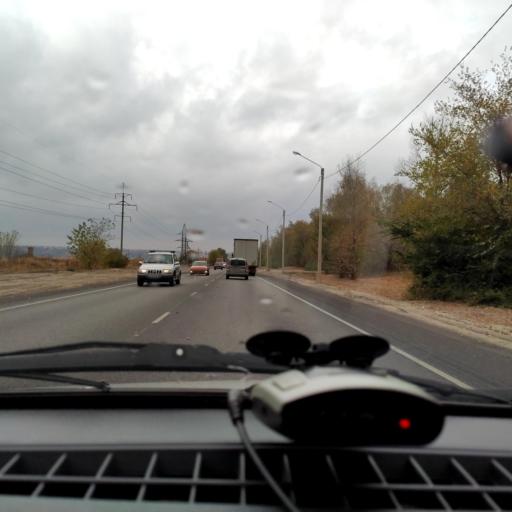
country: RU
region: Voronezj
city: Pridonskoy
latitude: 51.6977
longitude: 39.0834
